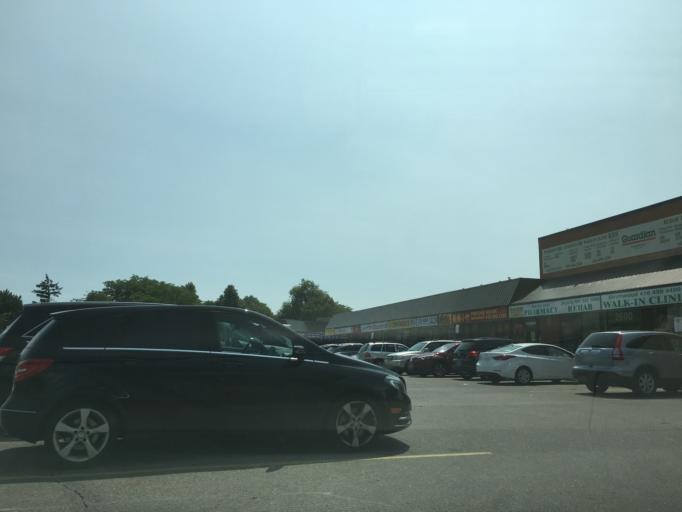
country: CA
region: Ontario
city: Scarborough
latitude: 43.7903
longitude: -79.3028
